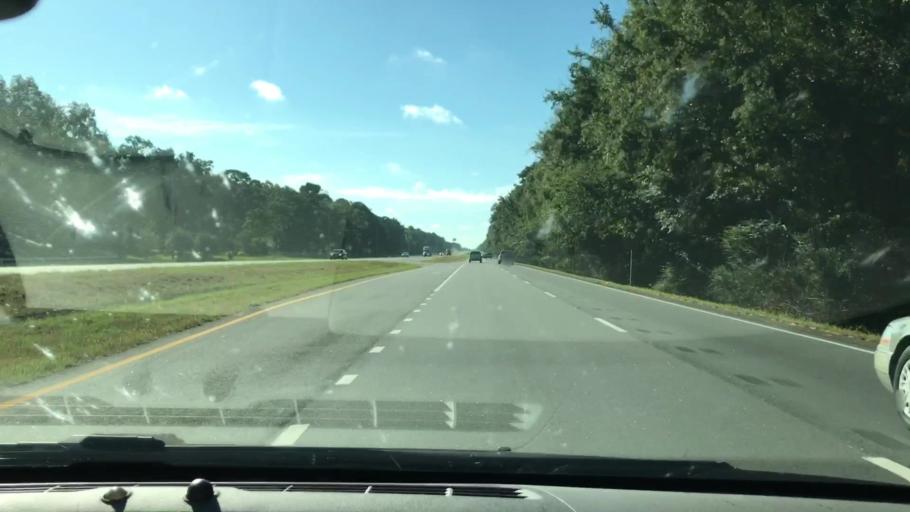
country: US
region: Georgia
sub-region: Lee County
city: Leesburg
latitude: 31.6586
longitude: -84.2738
